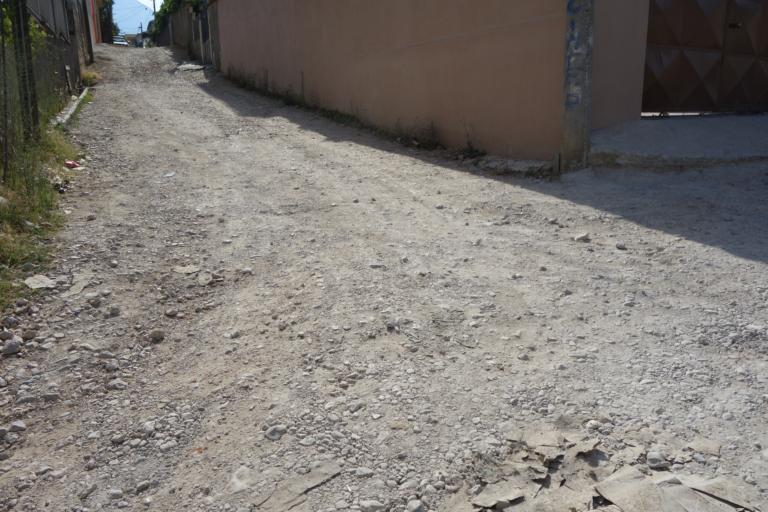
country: AL
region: Tirane
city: Tirana
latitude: 41.3353
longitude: 19.8446
